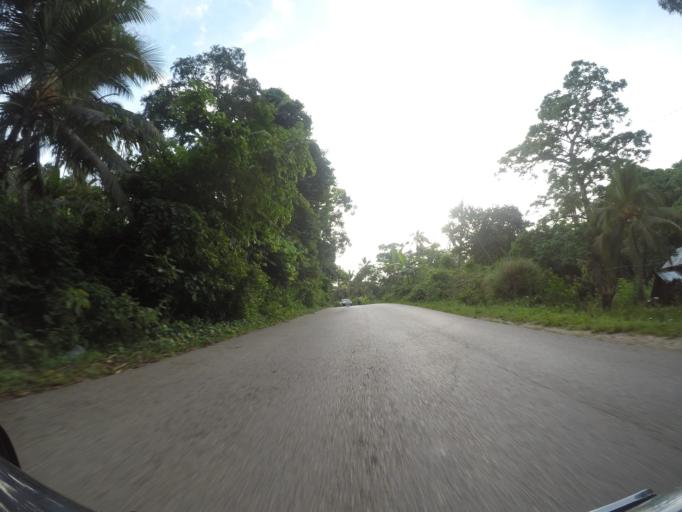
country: TZ
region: Pemba South
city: Chake Chake
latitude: -5.2764
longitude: 39.7698
